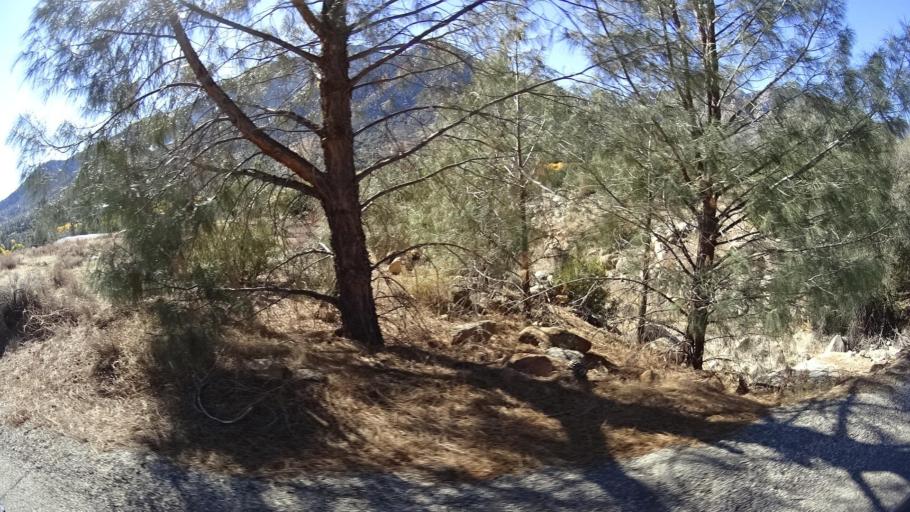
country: US
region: California
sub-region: Kern County
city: Kernville
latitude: 35.7738
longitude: -118.4315
